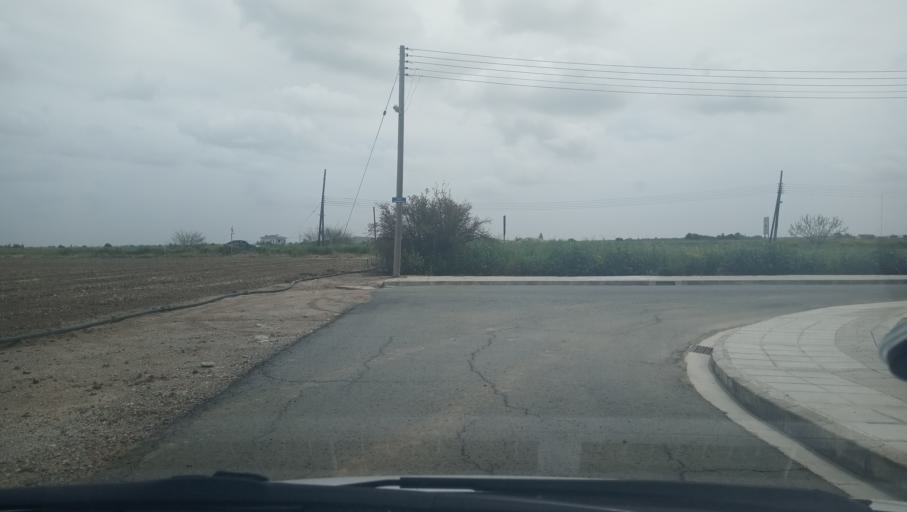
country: CY
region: Lefkosia
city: Pano Deftera
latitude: 35.0761
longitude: 33.2694
